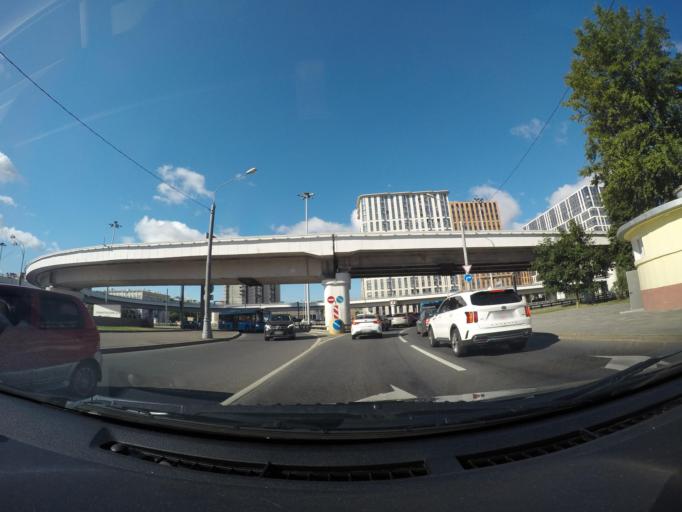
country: RU
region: Moskovskaya
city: Dorogomilovo
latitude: 55.7865
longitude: 37.5661
